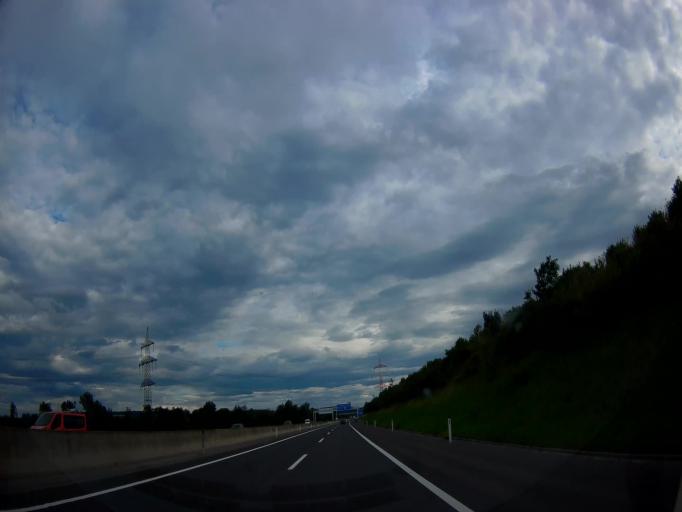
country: AT
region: Lower Austria
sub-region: Politischer Bezirk Sankt Polten
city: Traismauer
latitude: 48.3587
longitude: 15.7211
